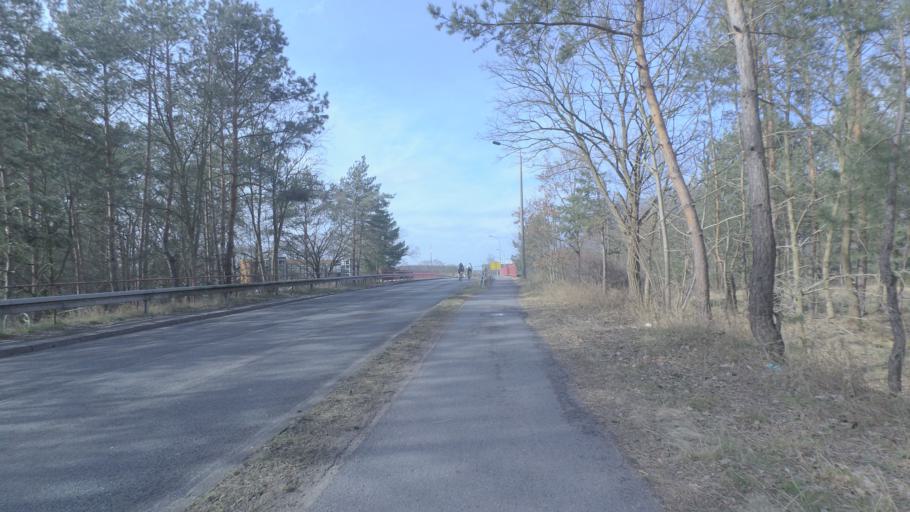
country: DE
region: Brandenburg
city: Ludwigsfelde
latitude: 52.3170
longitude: 13.2342
